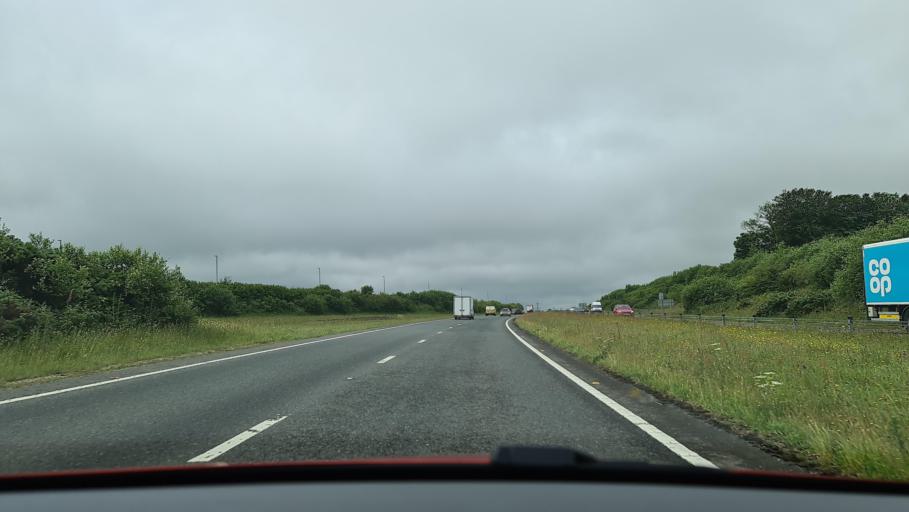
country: GB
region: England
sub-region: Cornwall
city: Roche
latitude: 50.4256
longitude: -4.8208
